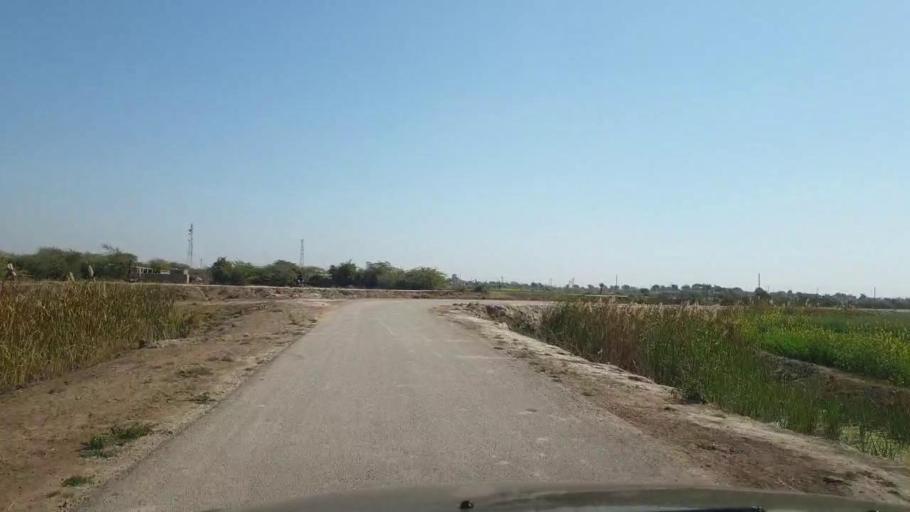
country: PK
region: Sindh
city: Mirpur Khas
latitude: 25.5696
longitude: 69.0600
